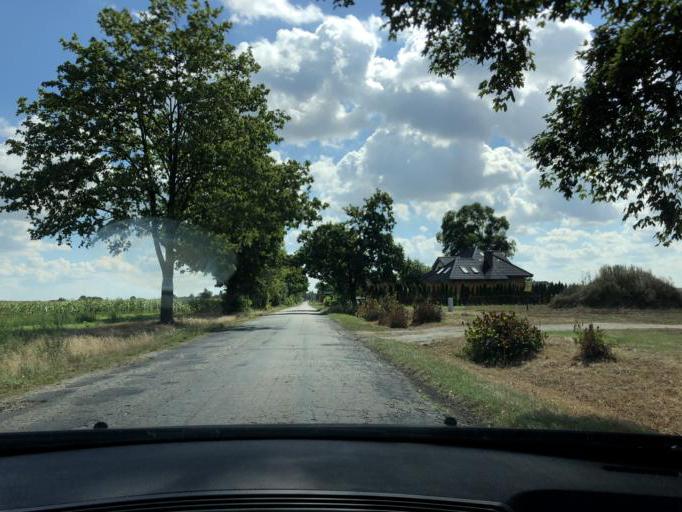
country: PL
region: Lodz Voivodeship
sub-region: Powiat wieruszowski
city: Czastary
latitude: 51.2379
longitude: 18.3399
